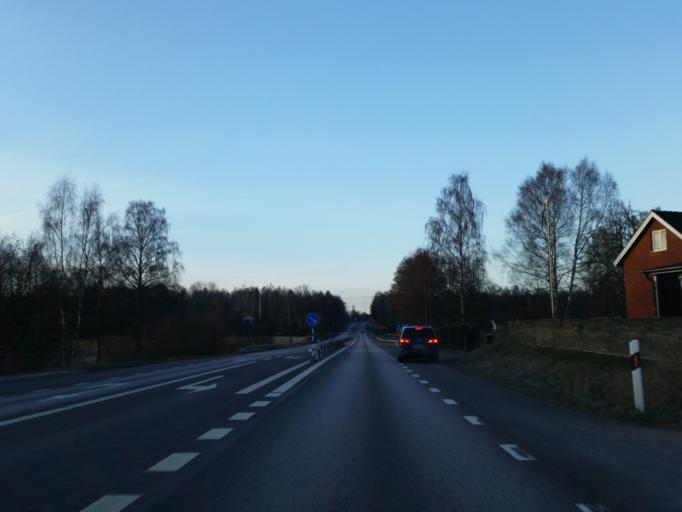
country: SE
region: Kalmar
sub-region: Oskarshamns Kommun
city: Oskarshamn
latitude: 57.4101
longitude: 16.4821
